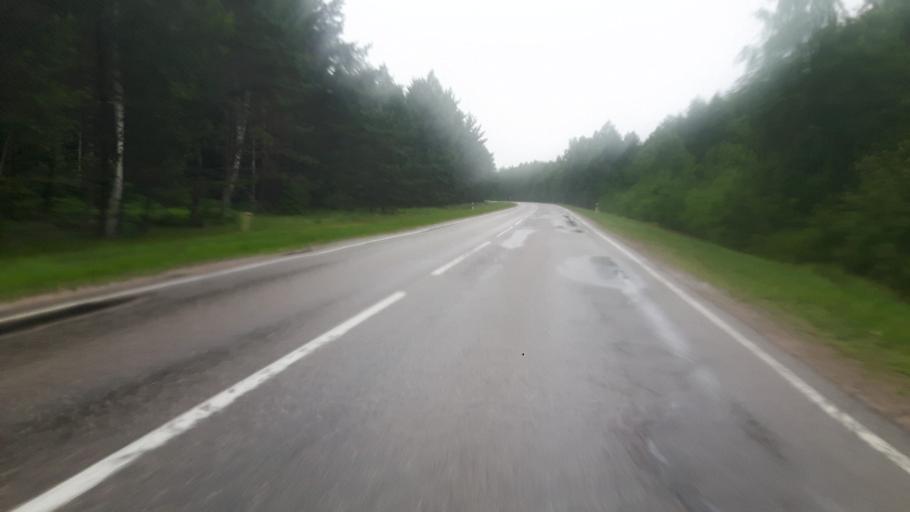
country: LV
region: Rucavas
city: Rucava
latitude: 56.1341
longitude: 21.1511
